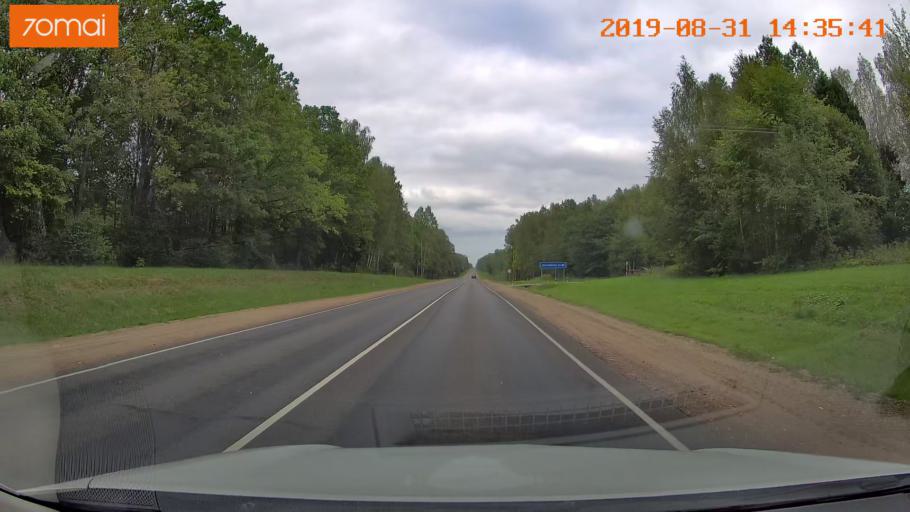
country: RU
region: Smolensk
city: Yekimovichi
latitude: 54.1645
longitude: 33.4614
